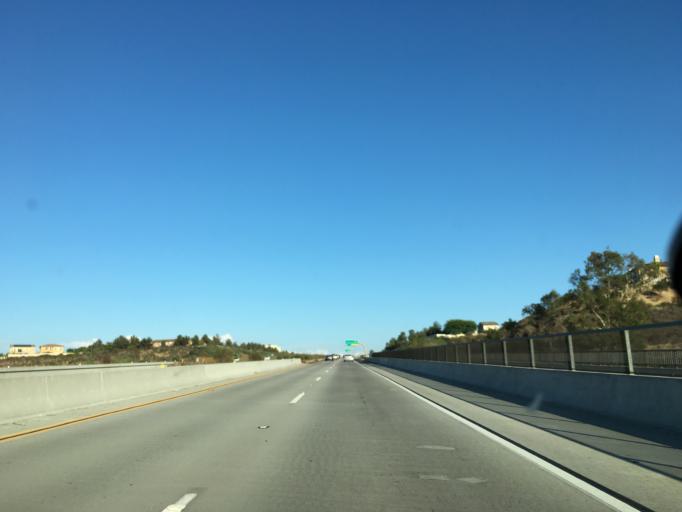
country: US
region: California
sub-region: San Diego County
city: Fairbanks Ranch
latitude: 32.9640
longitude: -117.1634
